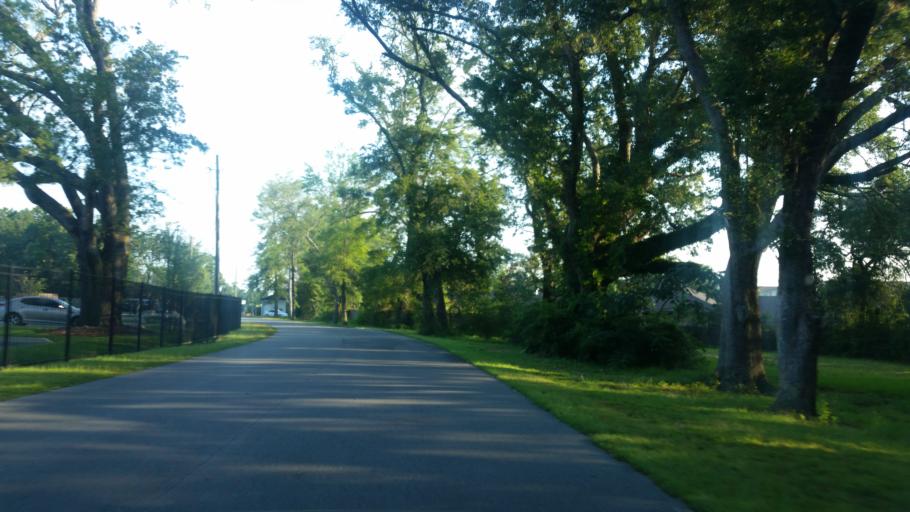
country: US
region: Florida
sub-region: Escambia County
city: Ferry Pass
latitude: 30.5384
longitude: -87.2160
